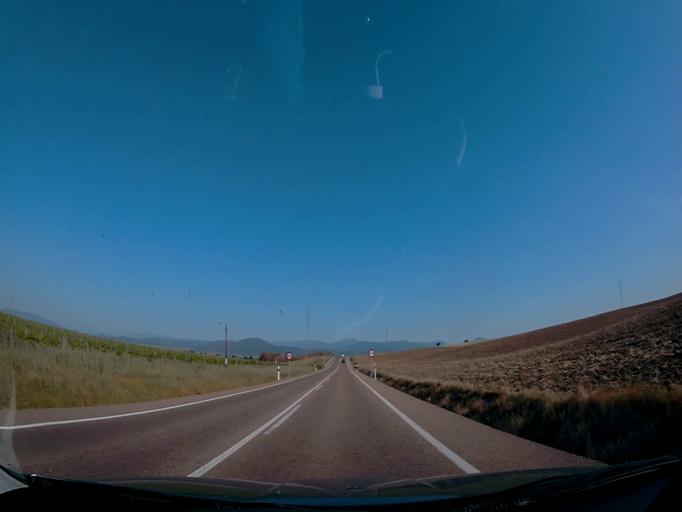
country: ES
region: Castille-La Mancha
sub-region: Province of Toledo
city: Hormigos
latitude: 40.1097
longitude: -4.4006
